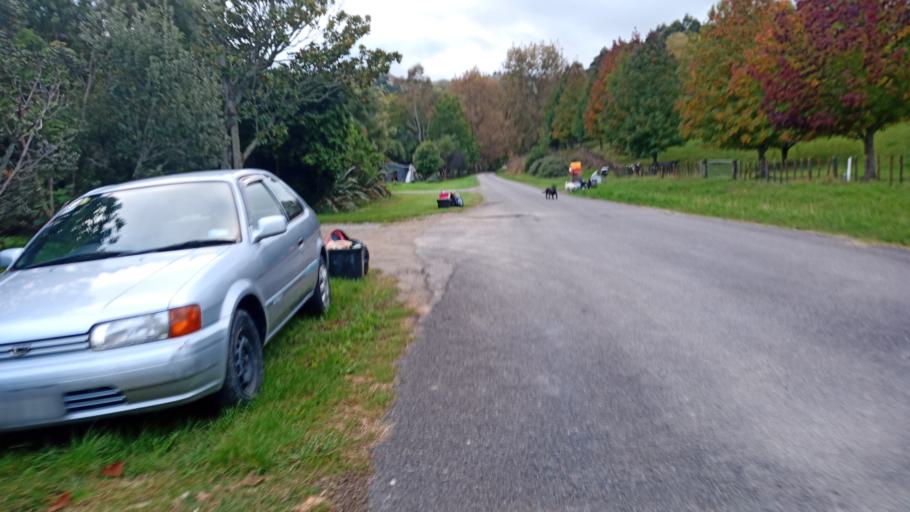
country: NZ
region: Gisborne
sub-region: Gisborne District
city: Gisborne
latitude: -38.6455
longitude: 178.0330
